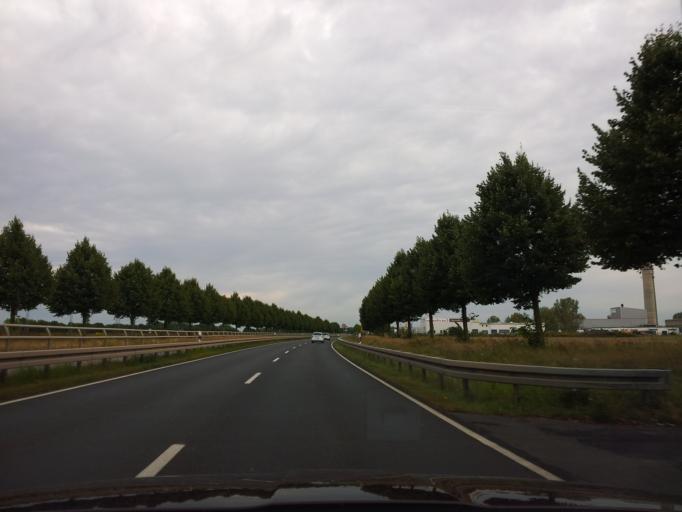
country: DE
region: Brandenburg
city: Ludwigsfelde
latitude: 52.3178
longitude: 13.2834
